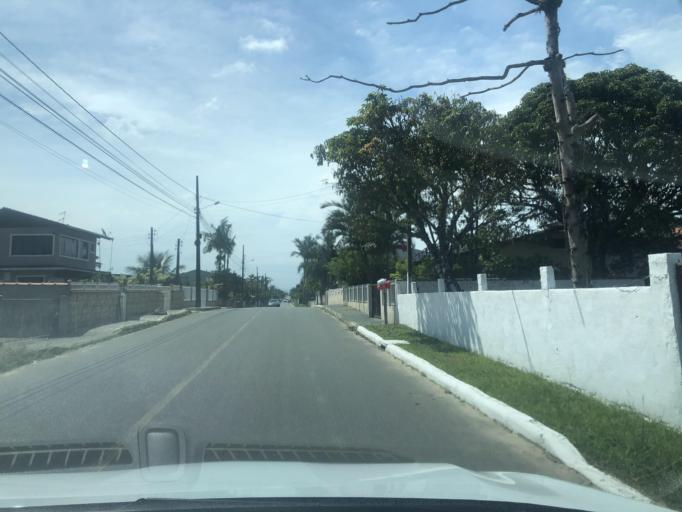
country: BR
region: Santa Catarina
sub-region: Sao Francisco Do Sul
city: Sao Francisco do Sul
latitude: -26.2122
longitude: -48.5349
